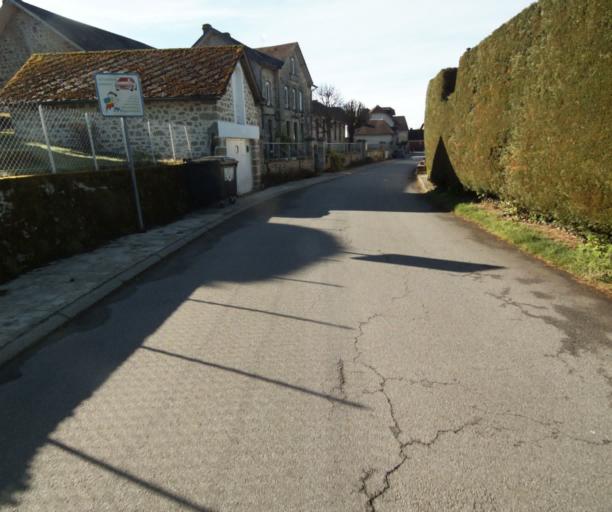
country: FR
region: Limousin
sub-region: Departement de la Correze
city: Laguenne
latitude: 45.2677
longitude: 1.8728
